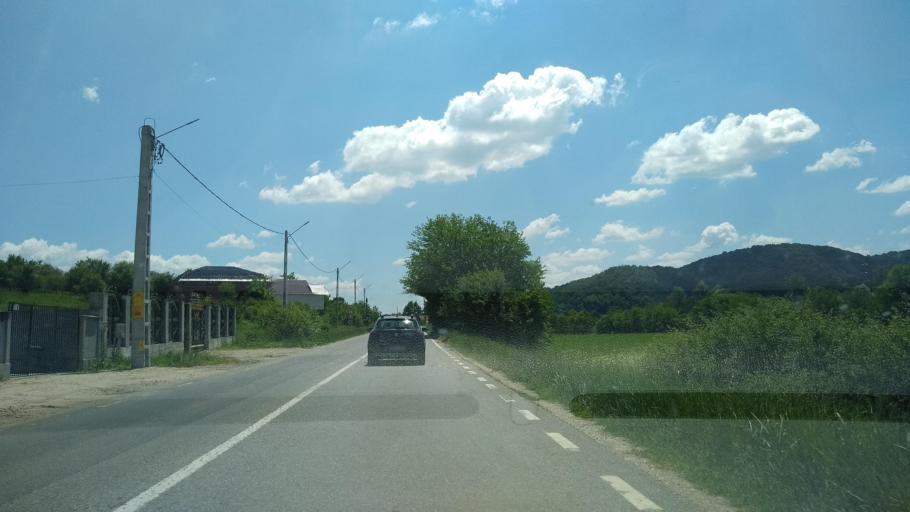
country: RO
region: Valcea
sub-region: Comuna Mihaesti
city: Mihaesti
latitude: 45.0597
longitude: 24.2430
